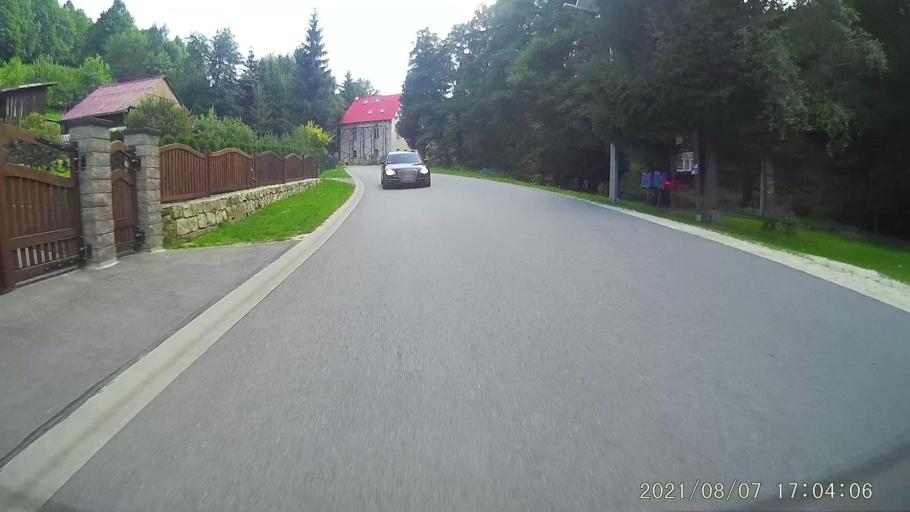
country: PL
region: Lower Silesian Voivodeship
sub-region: Powiat klodzki
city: Bystrzyca Klodzka
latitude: 50.2932
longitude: 16.5653
